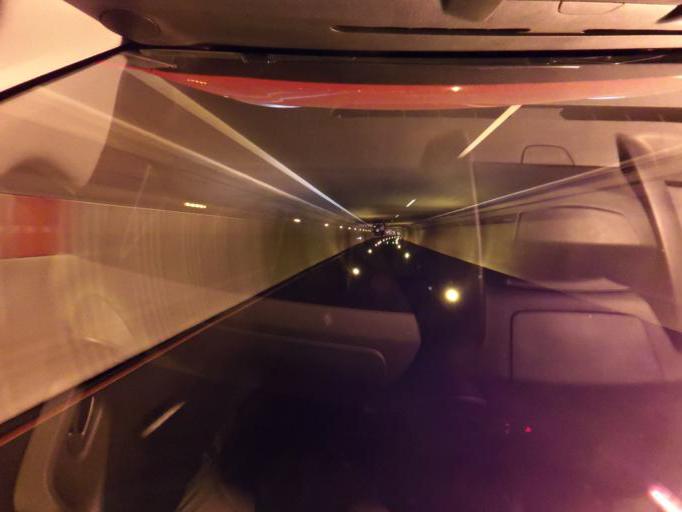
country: ES
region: Canary Islands
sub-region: Provincia de Las Palmas
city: Puerto Rico
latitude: 27.7938
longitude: -15.6988
